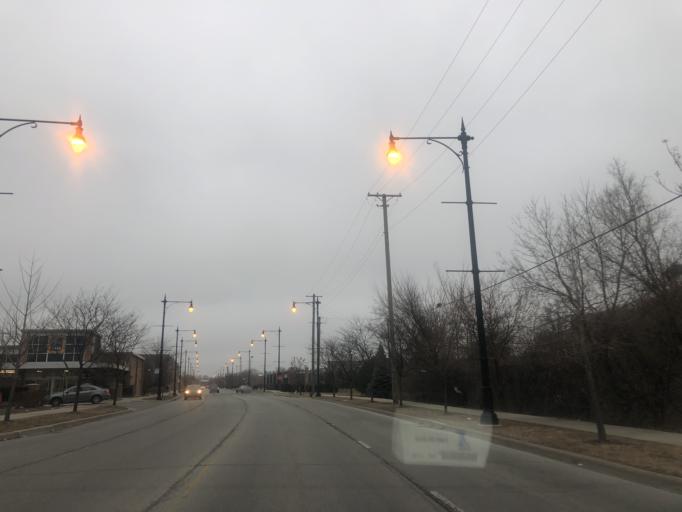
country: US
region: Illinois
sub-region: Cook County
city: Evergreen Park
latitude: 41.7384
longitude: -87.6320
